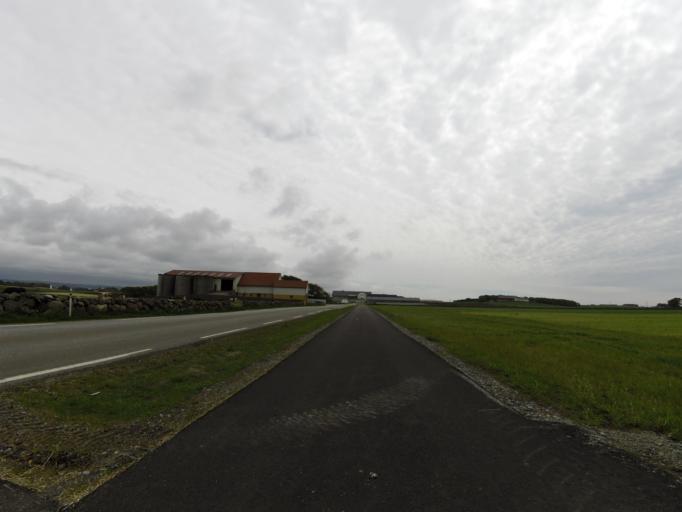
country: NO
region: Rogaland
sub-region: Ha
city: Naerbo
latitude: 58.6840
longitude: 5.5639
